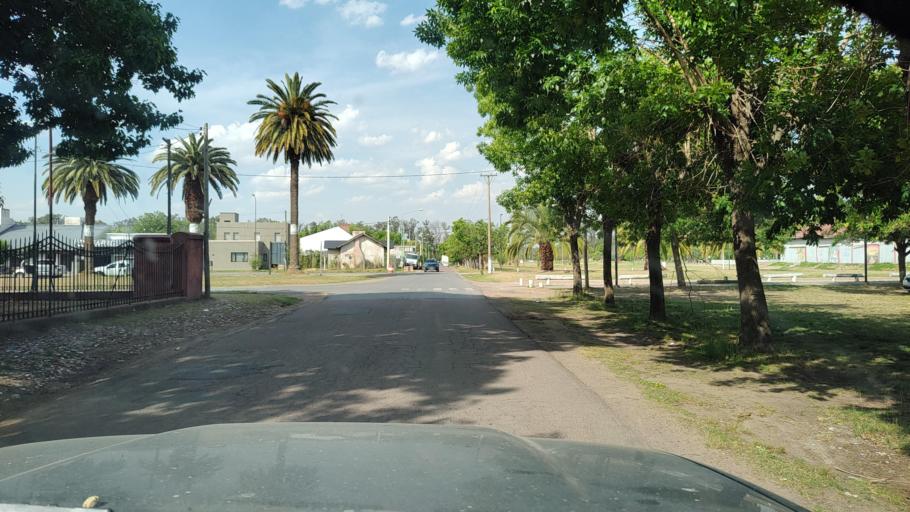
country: AR
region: Buenos Aires
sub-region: Partido de Lujan
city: Lujan
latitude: -34.6002
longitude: -59.1747
